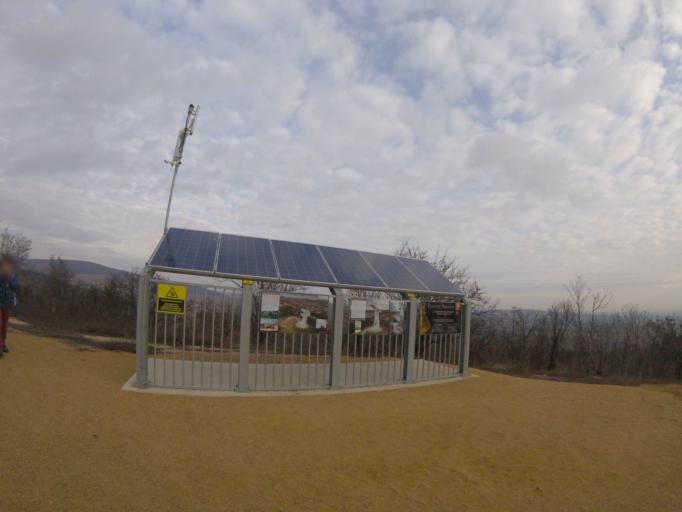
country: HU
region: Fejer
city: Velence
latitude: 47.2485
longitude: 18.6249
